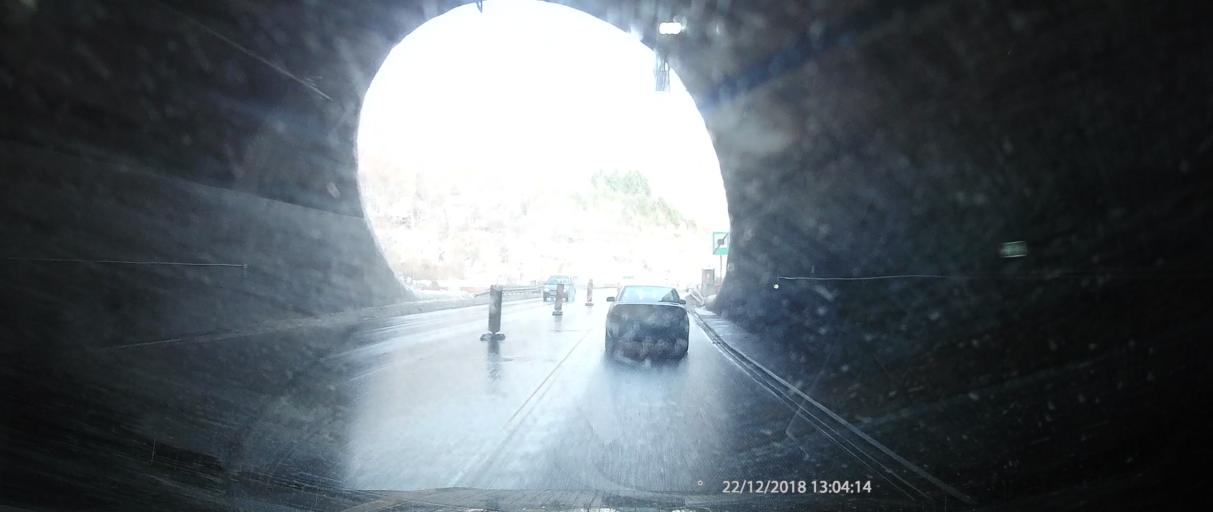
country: BG
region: Sofiya
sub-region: Obshtina Botevgrad
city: Botevgrad
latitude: 42.7877
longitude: 23.7965
